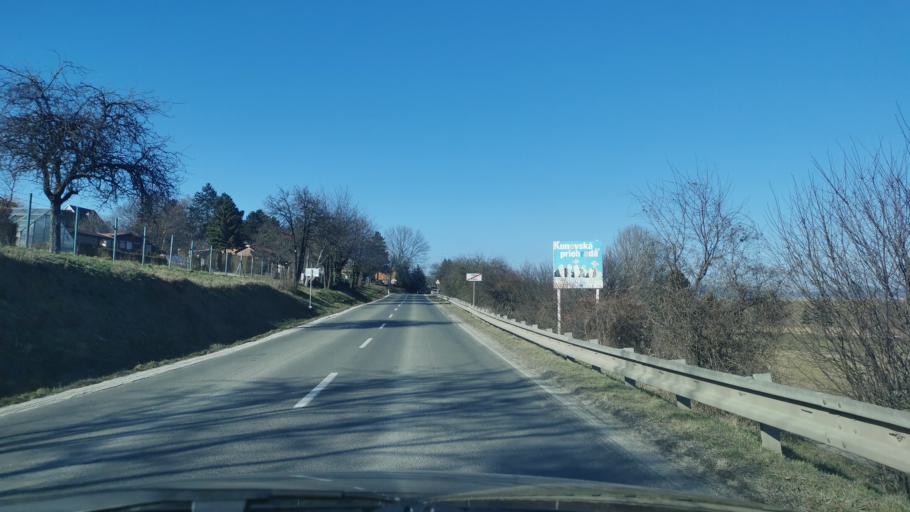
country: SK
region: Trnavsky
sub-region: Okres Senica
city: Senica
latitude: 48.7006
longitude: 17.4006
